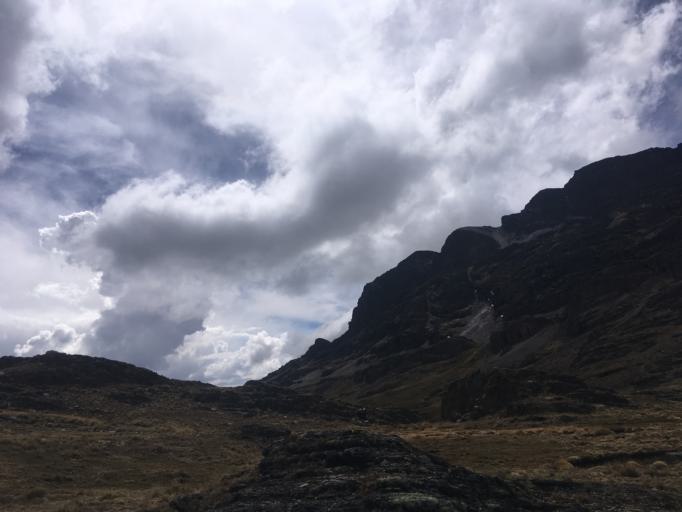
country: BO
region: La Paz
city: La Paz
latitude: -16.3934
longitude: -67.9626
